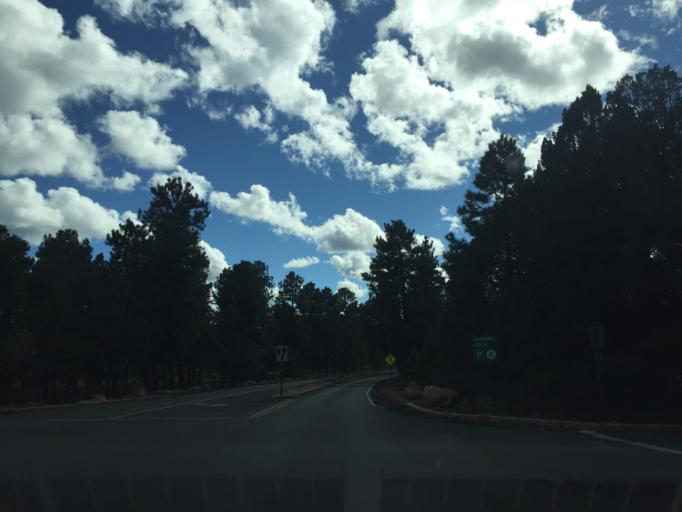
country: US
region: Arizona
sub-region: Coconino County
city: Grand Canyon
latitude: 36.0552
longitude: -112.1212
